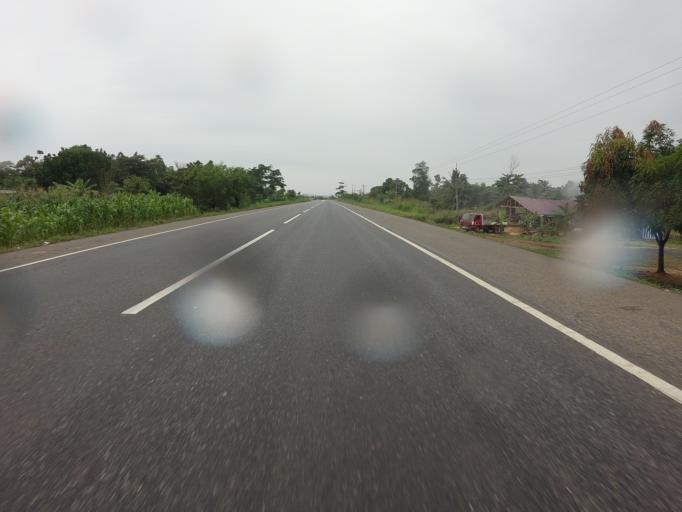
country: GH
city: Kibi
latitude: 6.1690
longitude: -0.4772
